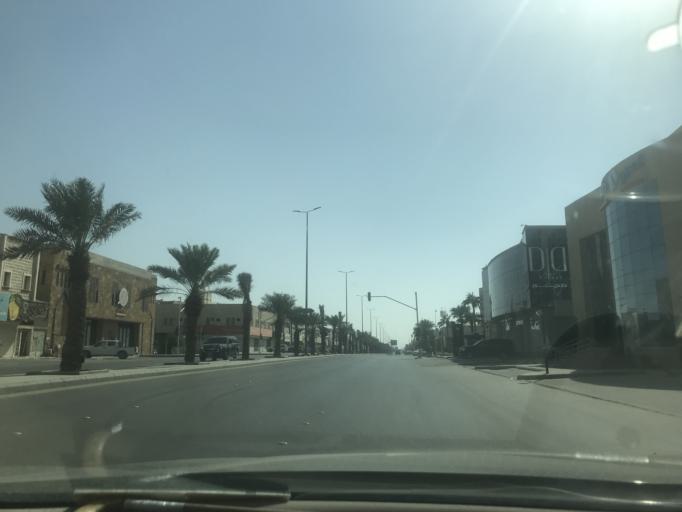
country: SA
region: Ar Riyad
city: Riyadh
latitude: 24.7374
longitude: 46.7611
